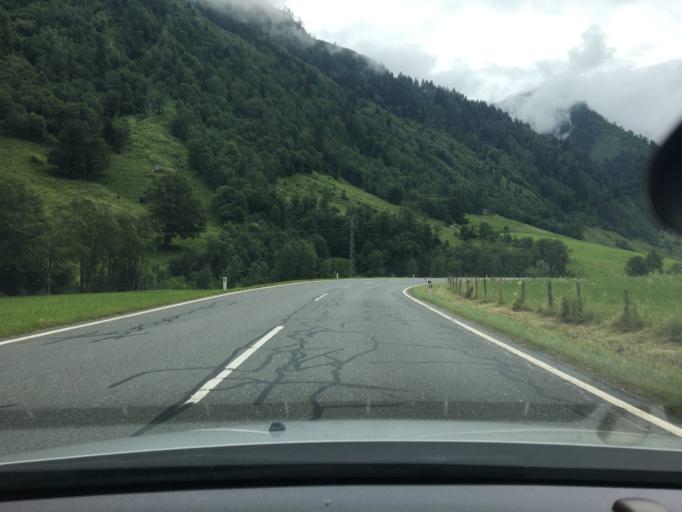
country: AT
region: Salzburg
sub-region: Politischer Bezirk Zell am See
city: Bruck an der Grossglocknerstrasse
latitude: 47.2501
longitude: 12.8270
